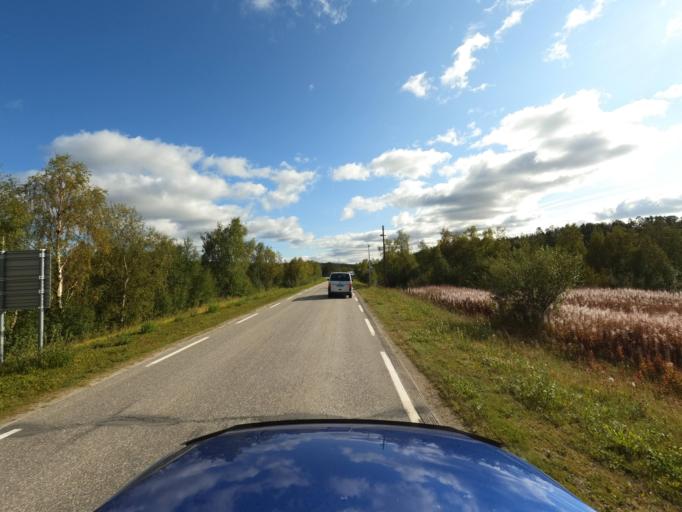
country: NO
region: Finnmark Fylke
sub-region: Karasjok
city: Karasjohka
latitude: 69.4000
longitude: 25.8277
